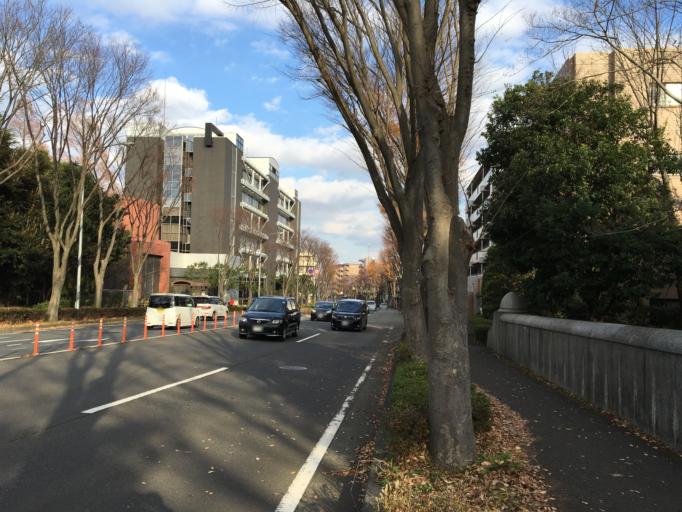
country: JP
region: Tokyo
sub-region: Machida-shi
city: Machida
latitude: 35.5400
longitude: 139.5653
